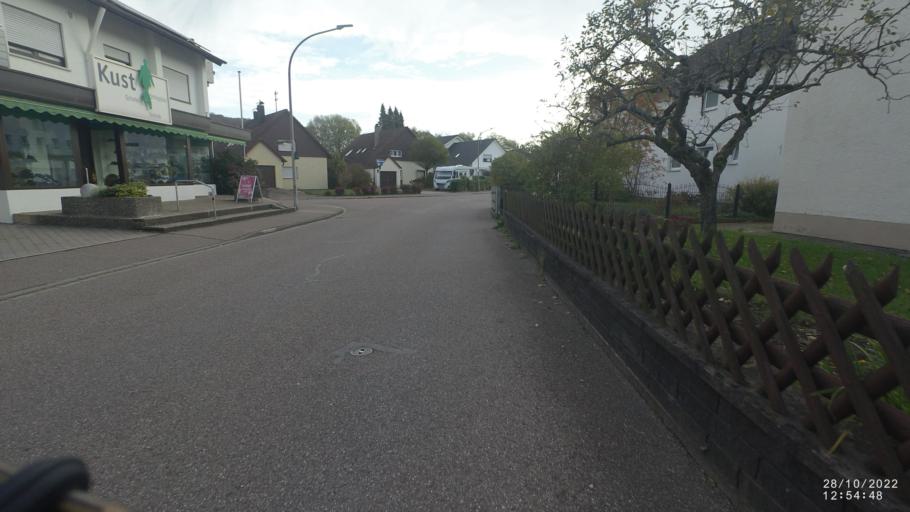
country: DE
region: Baden-Wuerttemberg
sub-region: Regierungsbezirk Stuttgart
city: Kuchen
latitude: 48.6417
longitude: 9.7958
